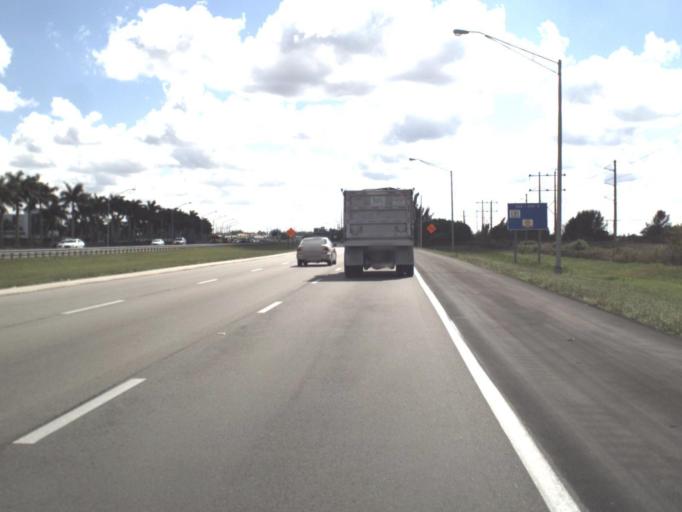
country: US
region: Florida
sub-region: Broward County
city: Tamarac
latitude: 26.2060
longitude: -80.2968
